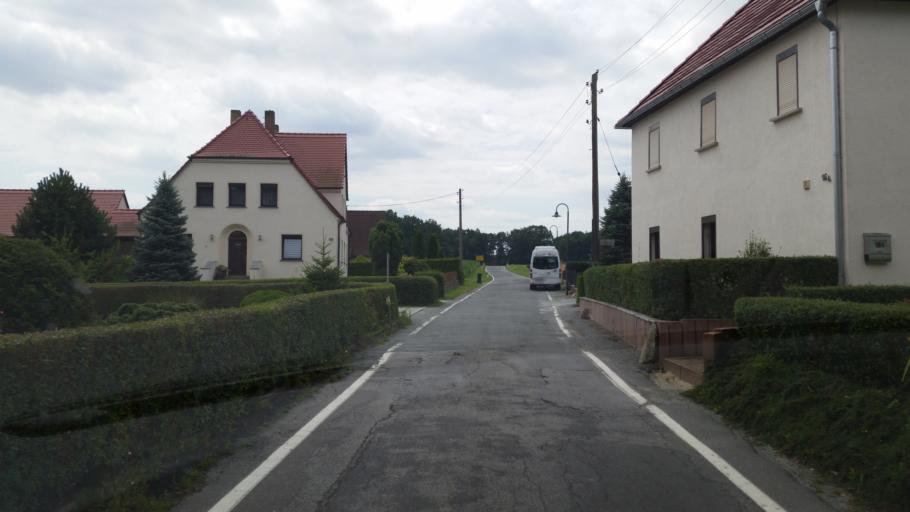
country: DE
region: Saxony
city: Neschwitz
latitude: 51.2292
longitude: 14.3344
